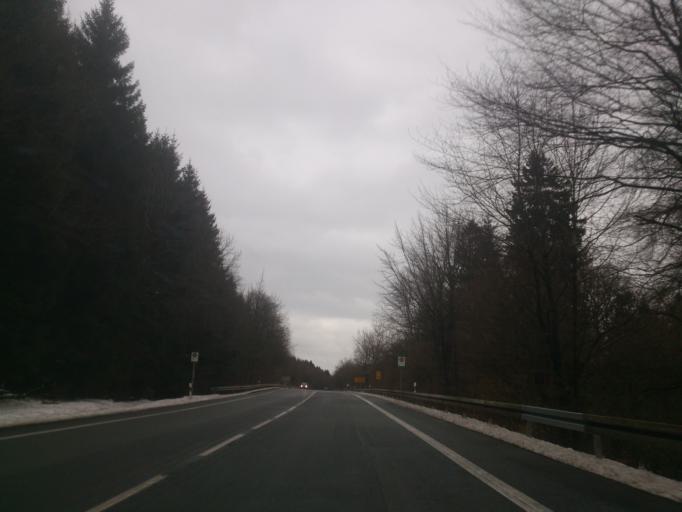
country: DE
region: North Rhine-Westphalia
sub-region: Regierungsbezirk Detmold
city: Bad Driburg
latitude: 51.6890
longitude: 8.9710
